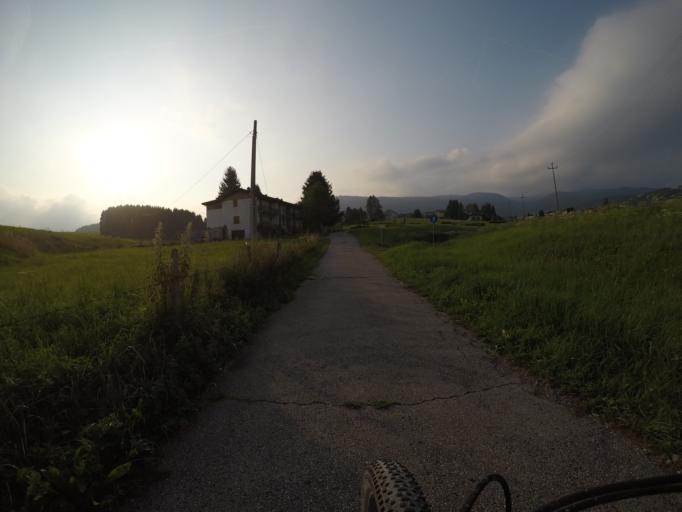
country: IT
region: Veneto
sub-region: Provincia di Vicenza
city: Asiago
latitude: 45.8811
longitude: 11.5006
